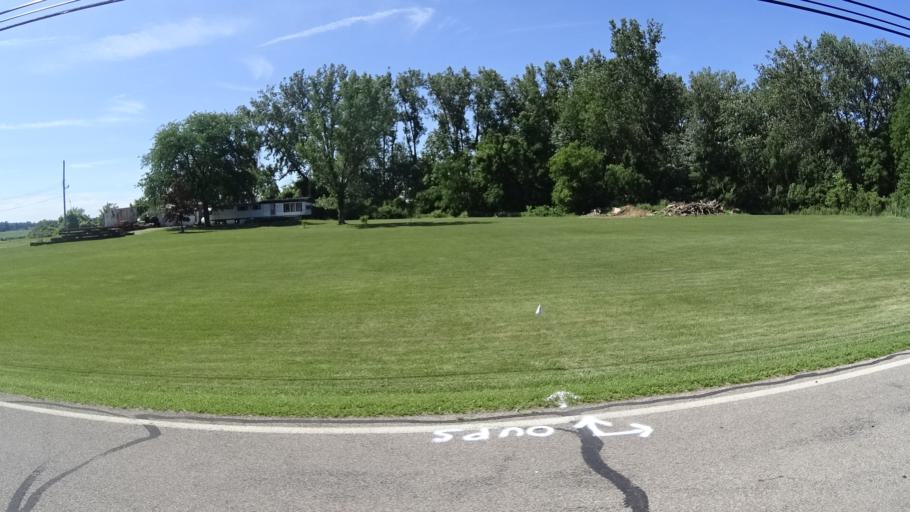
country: US
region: Ohio
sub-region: Ottawa County
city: Port Clinton
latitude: 41.4315
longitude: -82.8957
